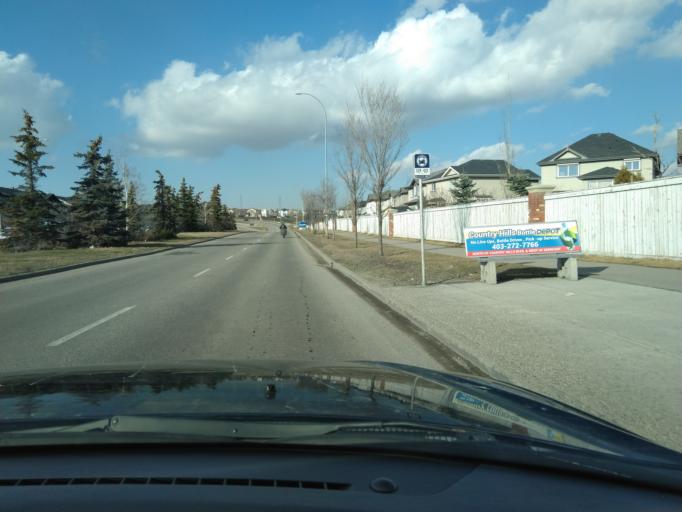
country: CA
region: Alberta
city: Calgary
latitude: 51.1645
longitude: -114.0700
